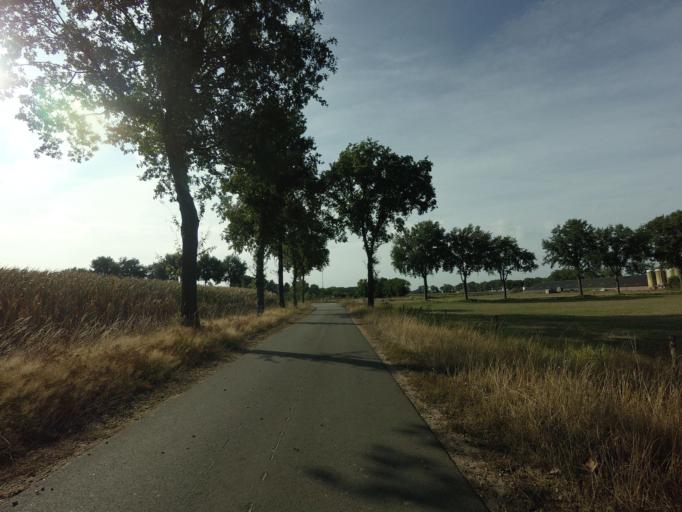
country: NL
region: North Brabant
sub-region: Gemeente Mill en Sint Hubert
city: Wilbertoord
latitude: 51.6635
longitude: 5.7590
